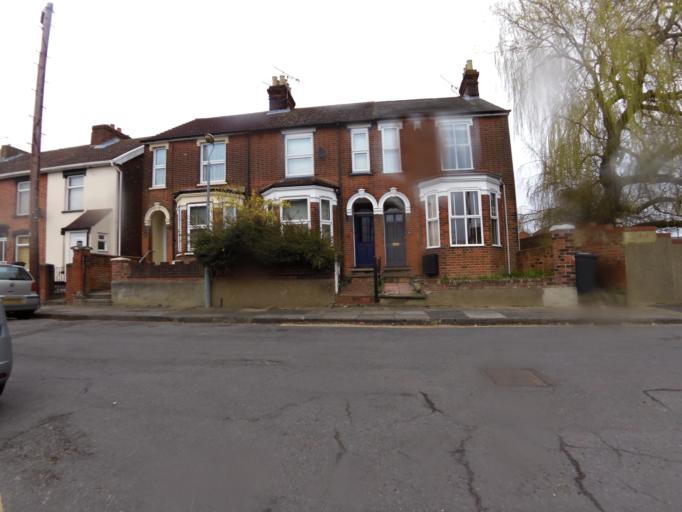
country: GB
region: England
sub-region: Suffolk
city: Ipswich
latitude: 52.0604
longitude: 1.1682
